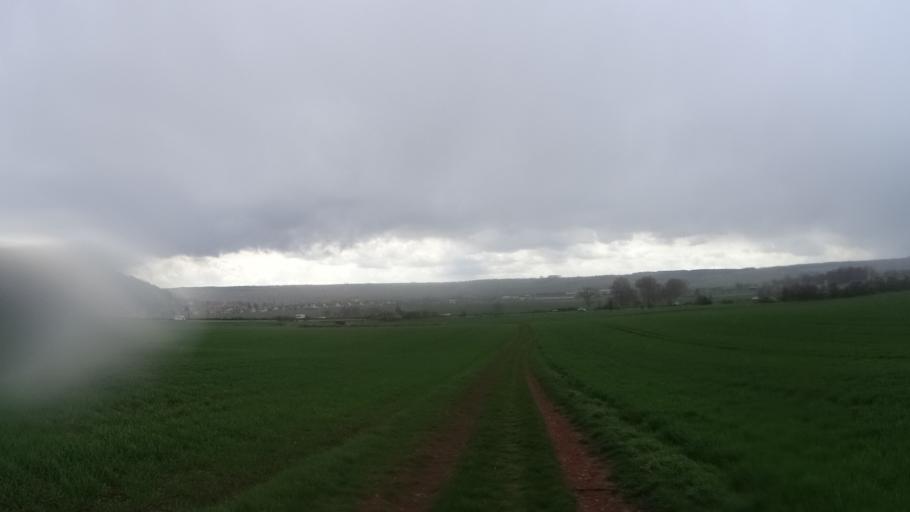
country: DE
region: Thuringia
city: Wandersleben
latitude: 50.8803
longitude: 10.8229
